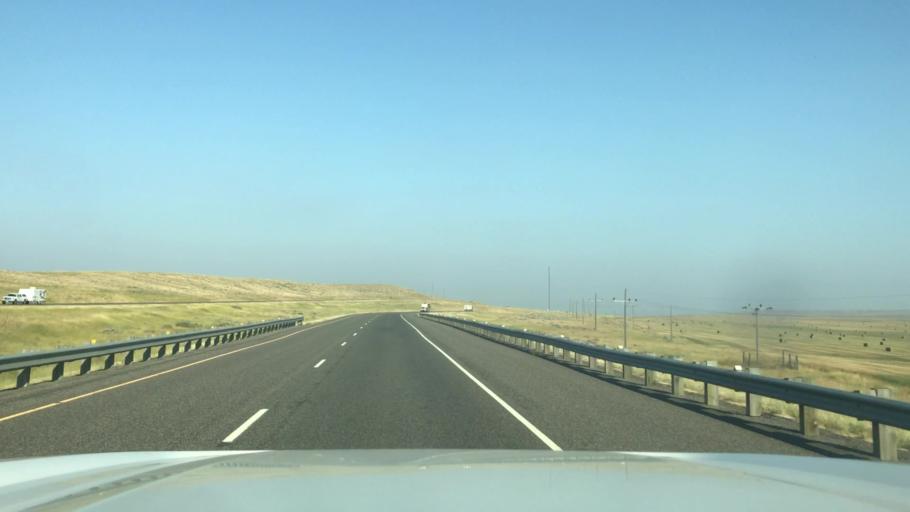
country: US
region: Montana
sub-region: Big Horn County
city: Hardin
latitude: 45.7605
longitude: -107.8744
